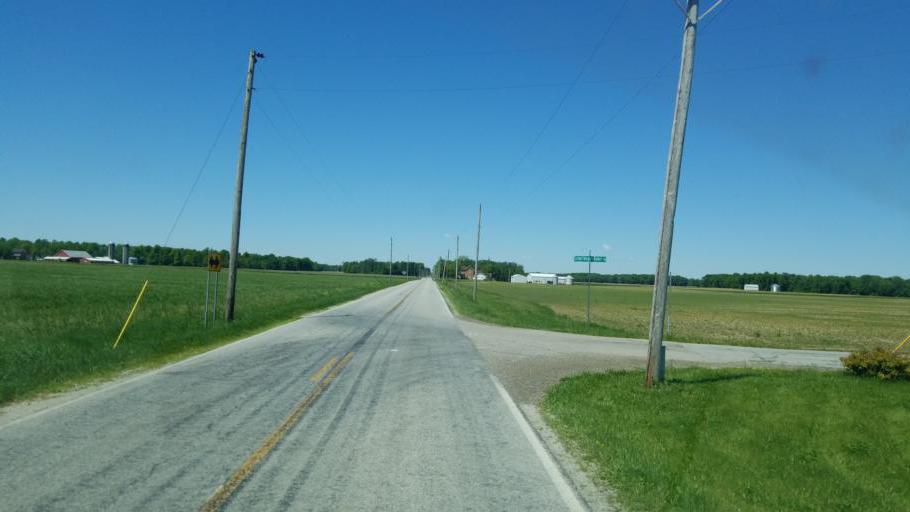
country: US
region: Ohio
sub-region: Shelby County
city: Fort Loramie
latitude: 40.3563
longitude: -84.3164
